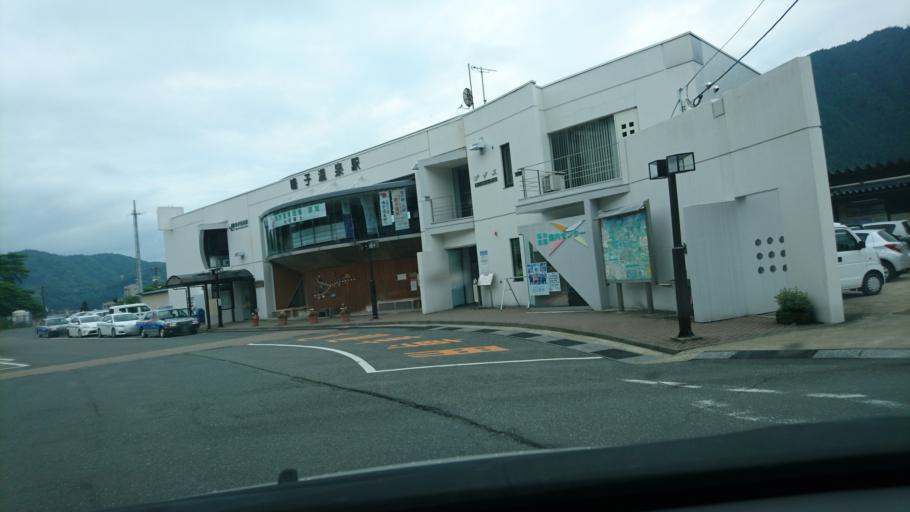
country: JP
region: Miyagi
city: Furukawa
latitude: 38.7432
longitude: 140.7164
